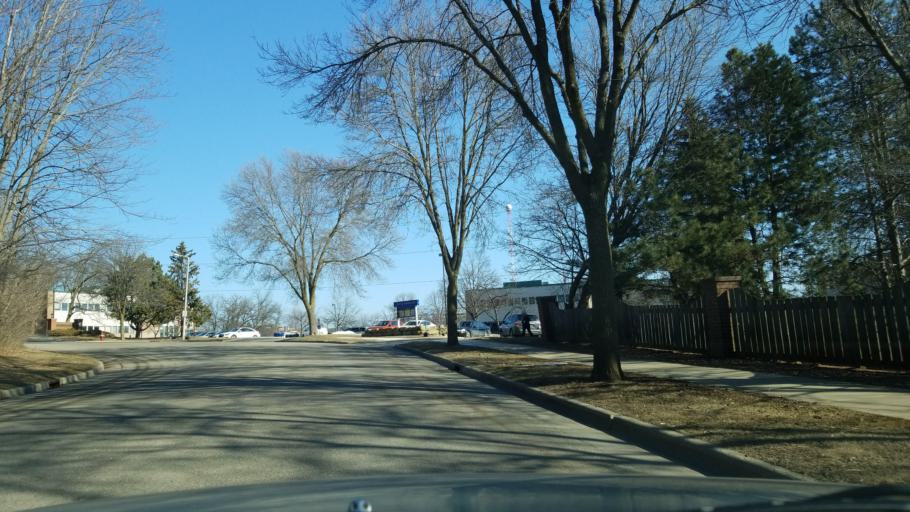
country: US
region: Wisconsin
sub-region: Dane County
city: Shorewood Hills
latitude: 43.0474
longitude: -89.4803
